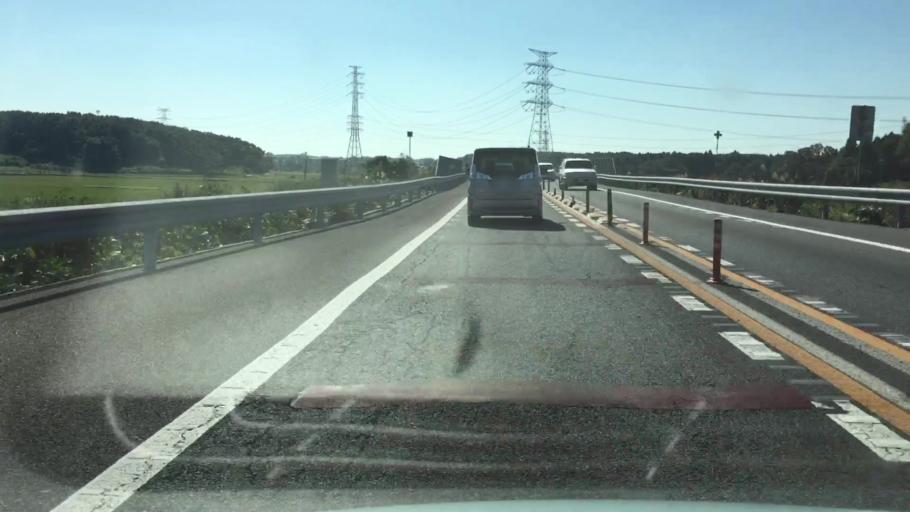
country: JP
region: Ibaraki
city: Ushiku
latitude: 36.0099
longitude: 140.1434
